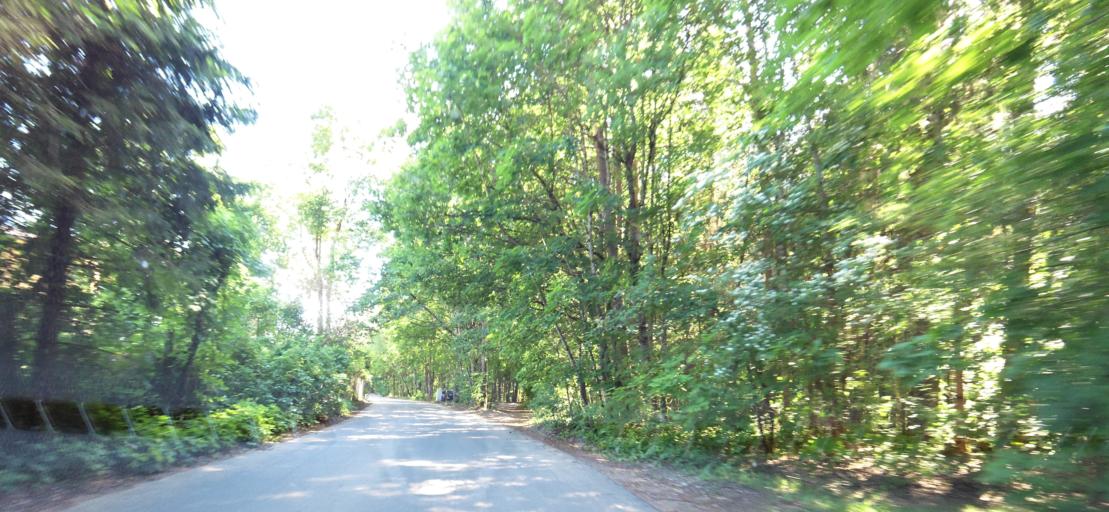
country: LT
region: Vilnius County
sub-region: Vilnius
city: Fabijoniskes
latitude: 54.8240
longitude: 25.3196
